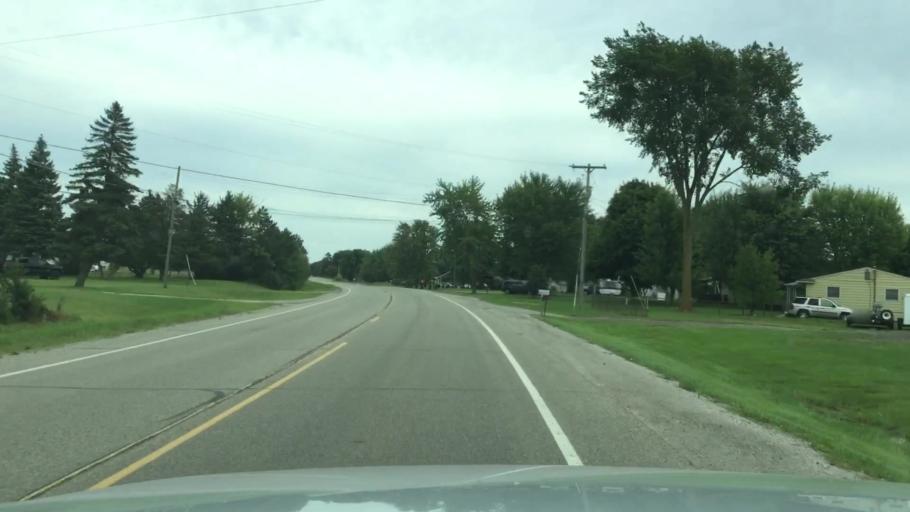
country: US
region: Michigan
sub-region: Shiawassee County
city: Durand
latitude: 42.9262
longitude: -83.9643
